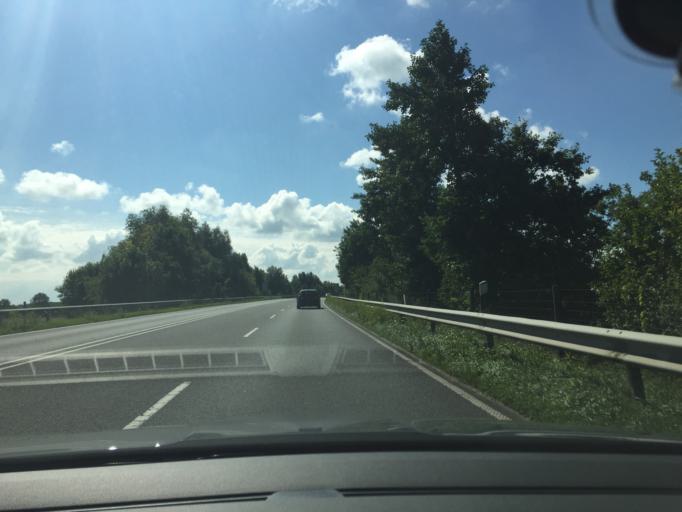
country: DE
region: Lower Saxony
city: Jever
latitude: 53.5808
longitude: 7.9248
